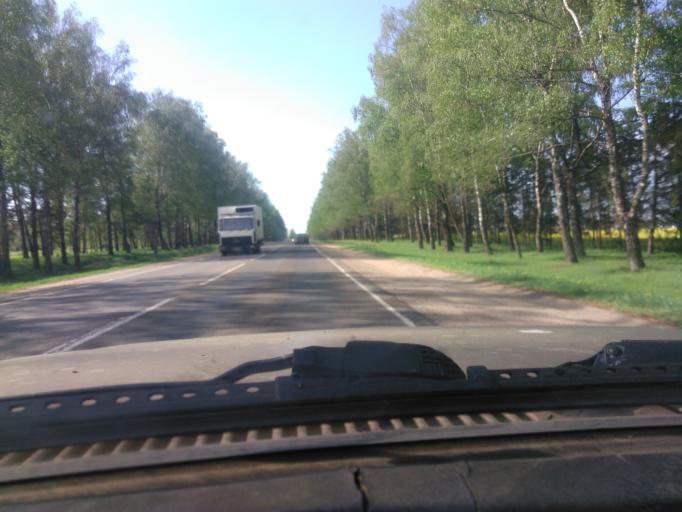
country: BY
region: Mogilev
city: Buynichy
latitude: 53.8460
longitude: 30.2509
